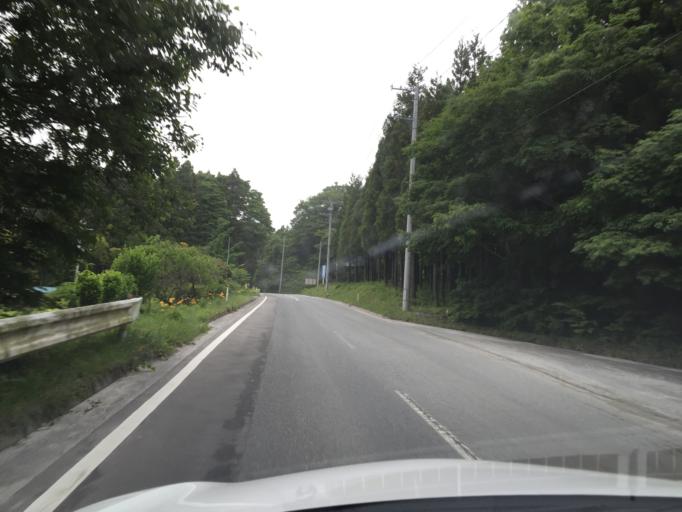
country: JP
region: Fukushima
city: Funehikimachi-funehiki
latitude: 37.3099
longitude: 140.7099
